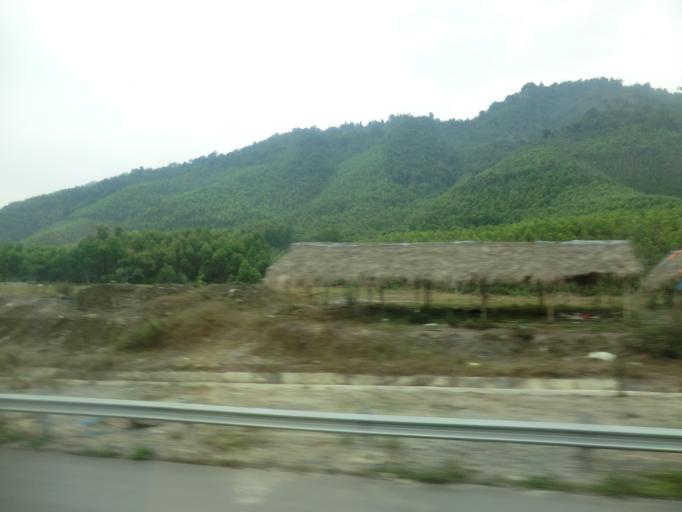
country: VN
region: Phu Tho
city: Ha Hoa
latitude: 21.5454
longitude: 104.9480
